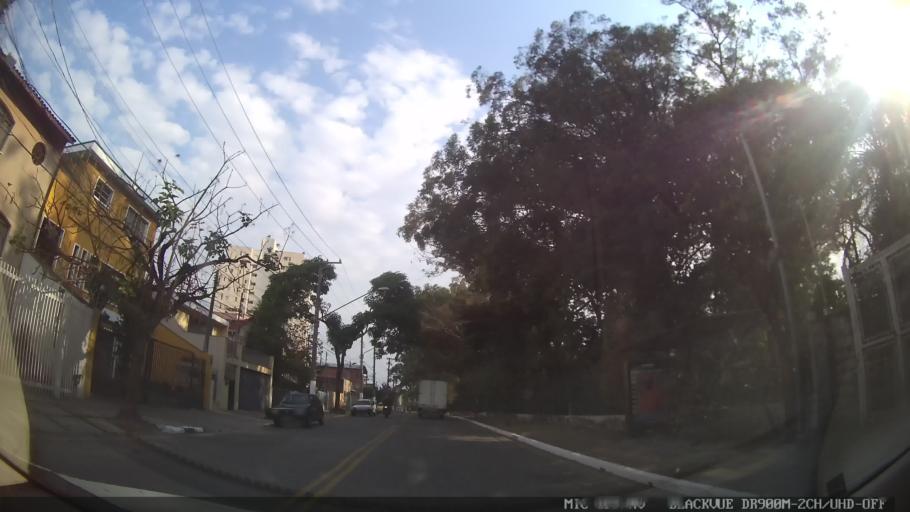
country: BR
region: Sao Paulo
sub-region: Sao Paulo
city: Sao Paulo
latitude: -23.5890
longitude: -46.6175
